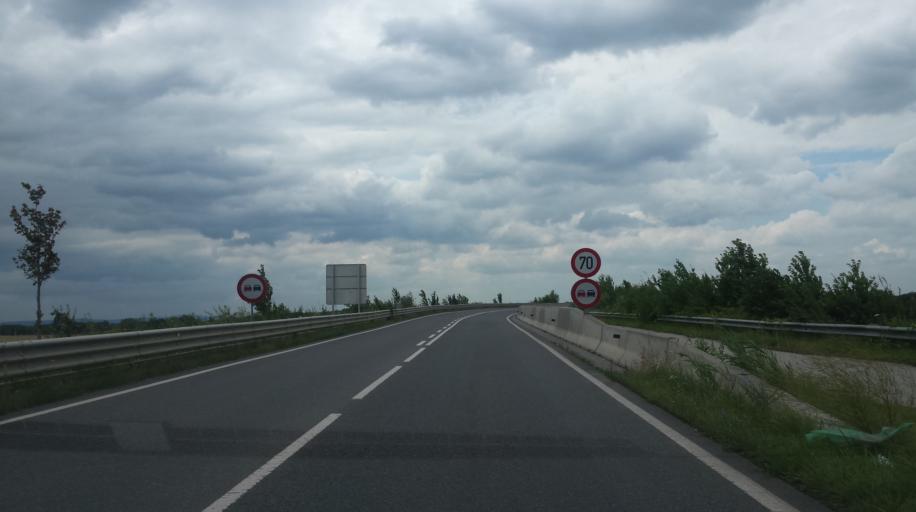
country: AT
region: Lower Austria
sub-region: Politischer Bezirk Wien-Umgebung
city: Himberg
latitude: 48.0693
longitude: 16.4580
